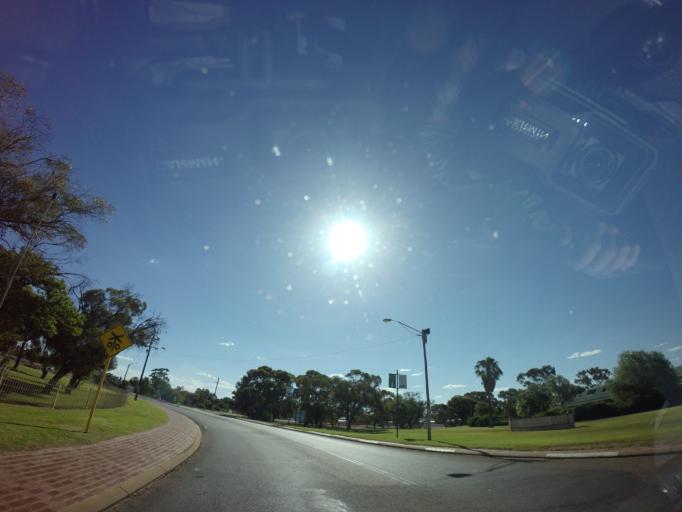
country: AU
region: Western Australia
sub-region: Merredin
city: Merredin
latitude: -31.4815
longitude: 118.2732
